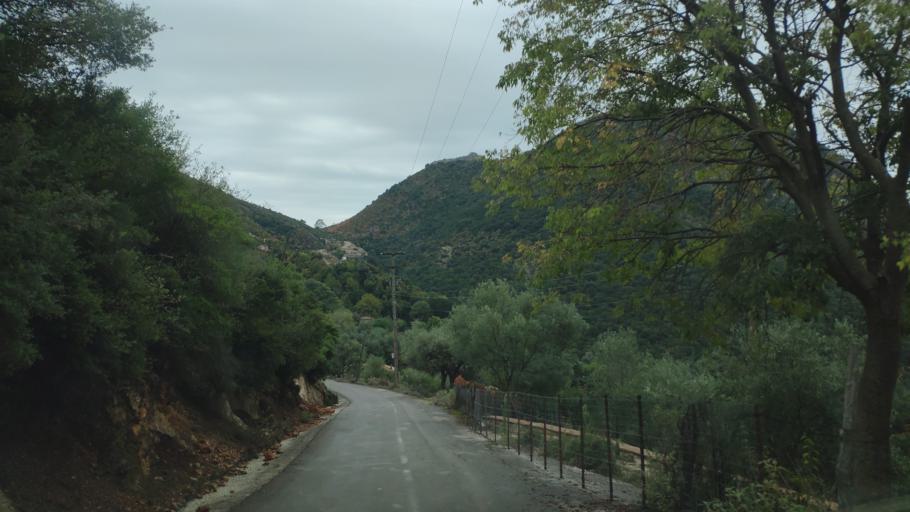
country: GR
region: Epirus
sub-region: Nomos Prevezis
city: Kanalaki
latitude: 39.3475
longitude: 20.6491
